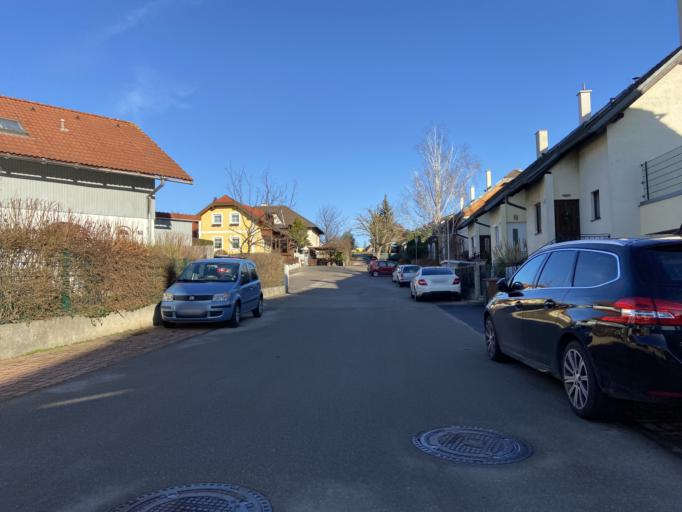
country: AT
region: Lower Austria
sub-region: Politischer Bezirk Modling
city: Neu-Guntramsdorf
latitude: 48.0606
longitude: 16.3160
